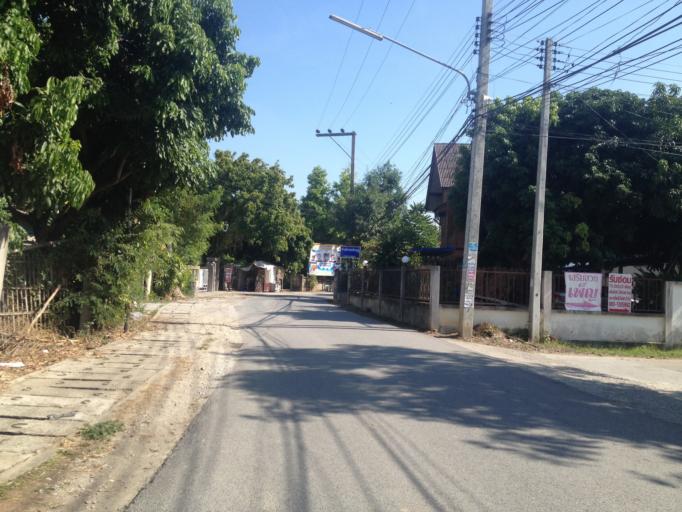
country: TH
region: Chiang Mai
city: Hang Dong
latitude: 18.6920
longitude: 98.9442
